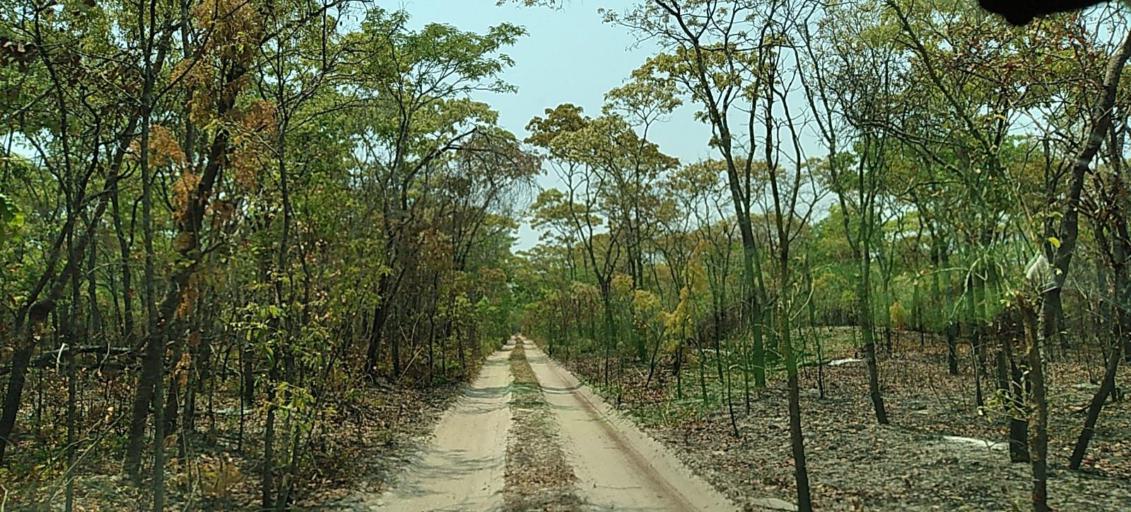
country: ZM
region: North-Western
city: Kabompo
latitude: -13.6502
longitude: 24.4743
